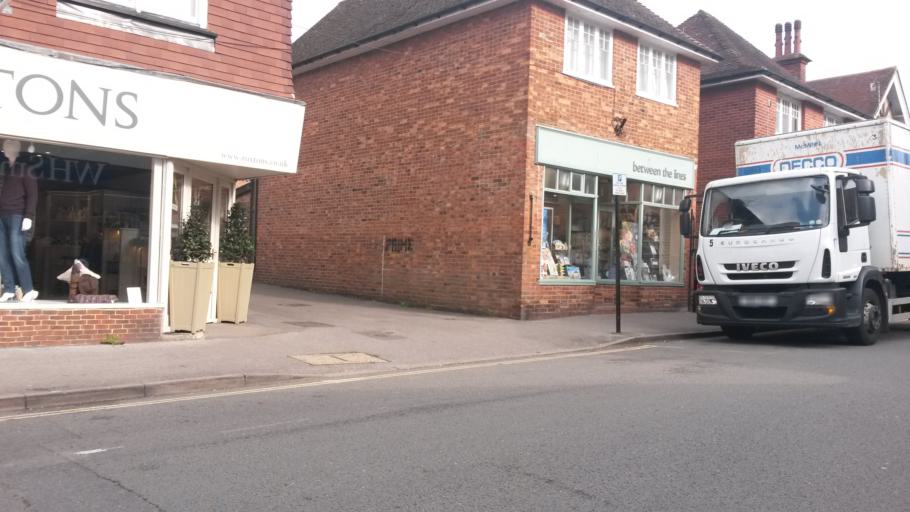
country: GB
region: England
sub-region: Surrey
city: Haslemere
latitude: 51.0888
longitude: -0.7101
